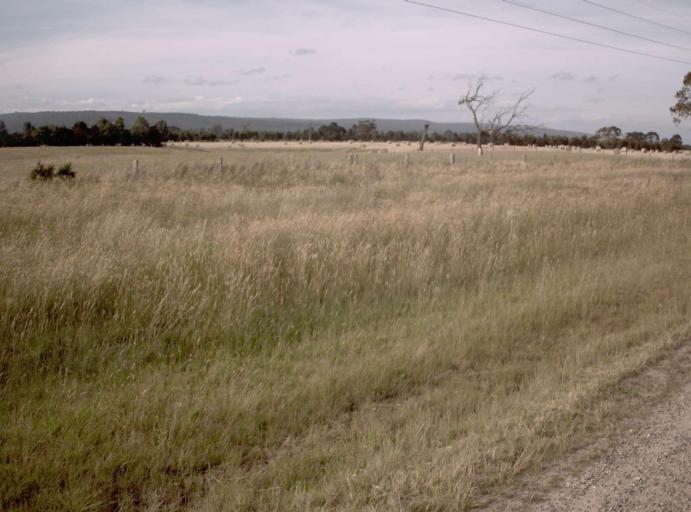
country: AU
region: Victoria
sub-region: Latrobe
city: Traralgon
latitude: -38.1123
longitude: 146.5840
